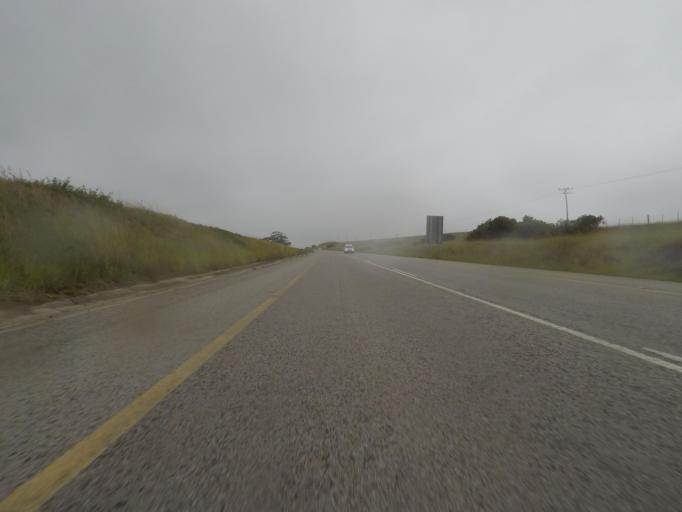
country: ZA
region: Eastern Cape
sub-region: Cacadu District Municipality
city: Grahamstown
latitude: -33.6366
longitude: 26.3206
